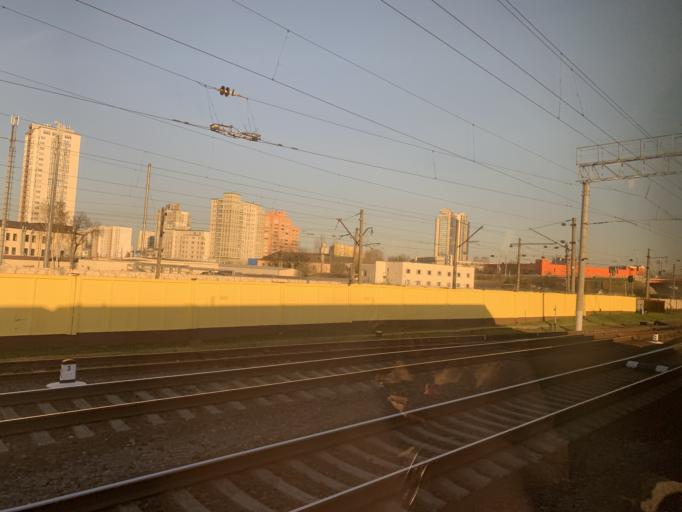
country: BY
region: Minsk
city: Minsk
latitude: 53.9117
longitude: 27.5223
